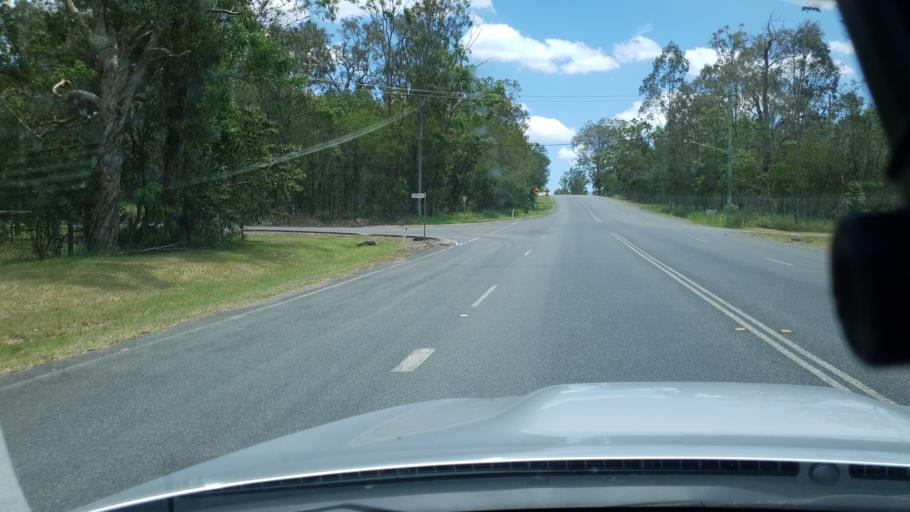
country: AU
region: Queensland
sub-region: Logan
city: North Maclean
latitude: -27.7677
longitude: 152.9839
